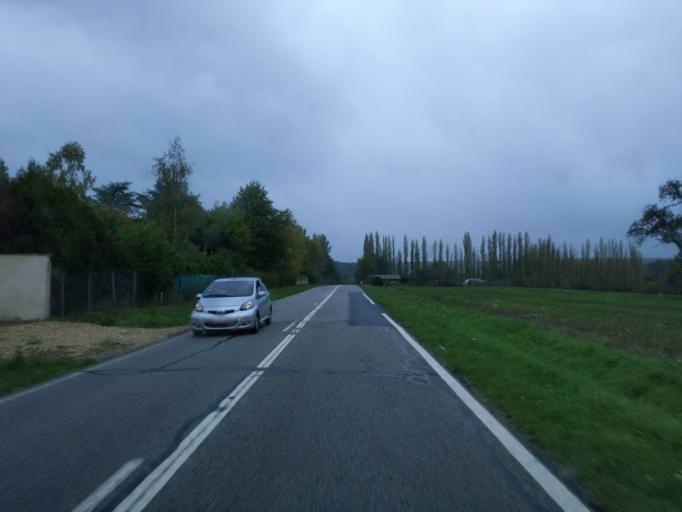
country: FR
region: Ile-de-France
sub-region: Departement des Yvelines
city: Dampierre-en-Yvelines
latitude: 48.6952
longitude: 1.9771
